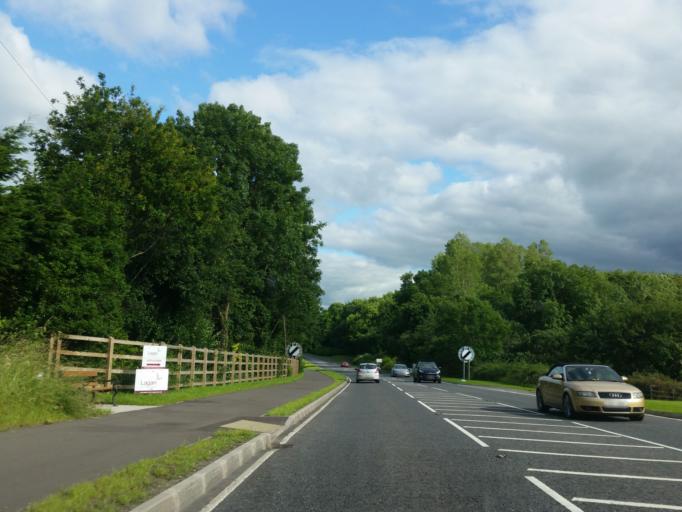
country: GB
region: Northern Ireland
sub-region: Fermanagh District
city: Enniskillen
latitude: 54.3283
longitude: -7.6167
